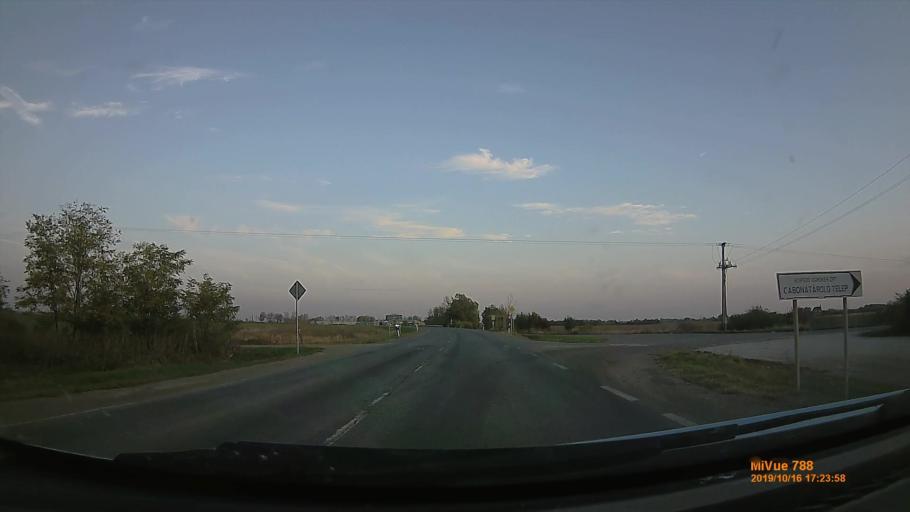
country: HU
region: Heves
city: Fuzesabony
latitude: 47.7686
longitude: 20.3841
